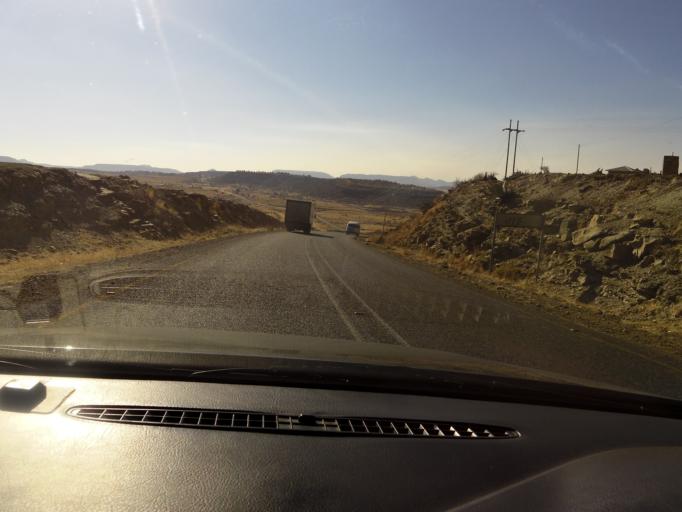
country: LS
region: Mohale's Hoek District
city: Mohale's Hoek
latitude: -30.0623
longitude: 27.4152
